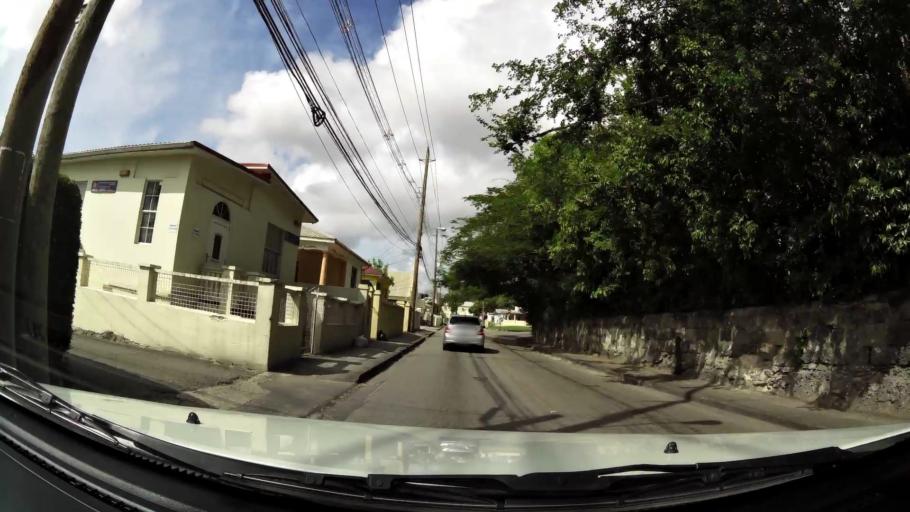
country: BB
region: Saint Michael
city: Bridgetown
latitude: 13.1038
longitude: -59.6016
